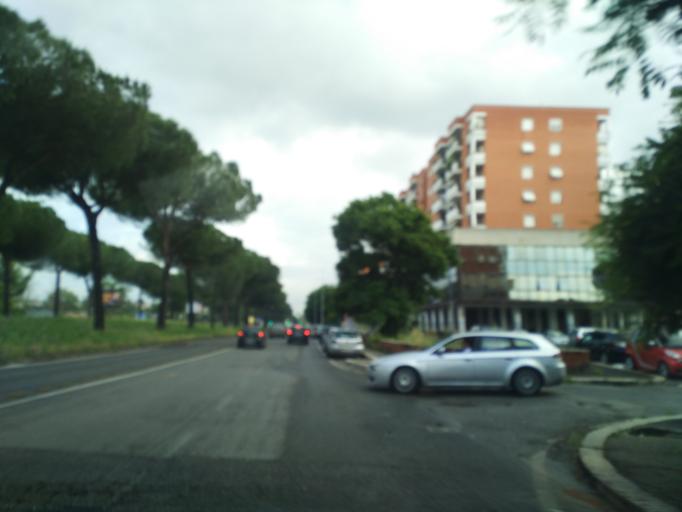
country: IT
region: Latium
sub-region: Citta metropolitana di Roma Capitale
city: Rome
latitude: 41.9178
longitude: 12.5678
